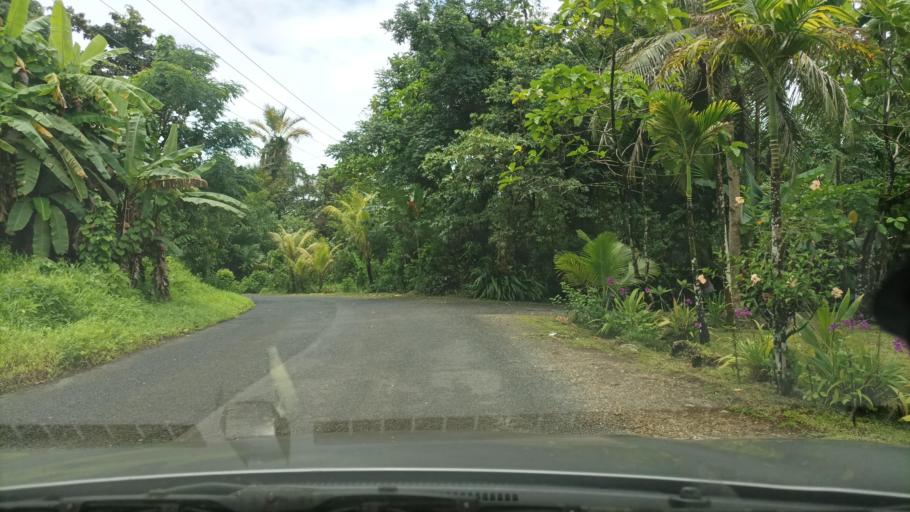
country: FM
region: Pohnpei
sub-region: Madolenihm Municipality
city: Madolenihm Municipality Government
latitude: 6.8482
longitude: 158.3009
